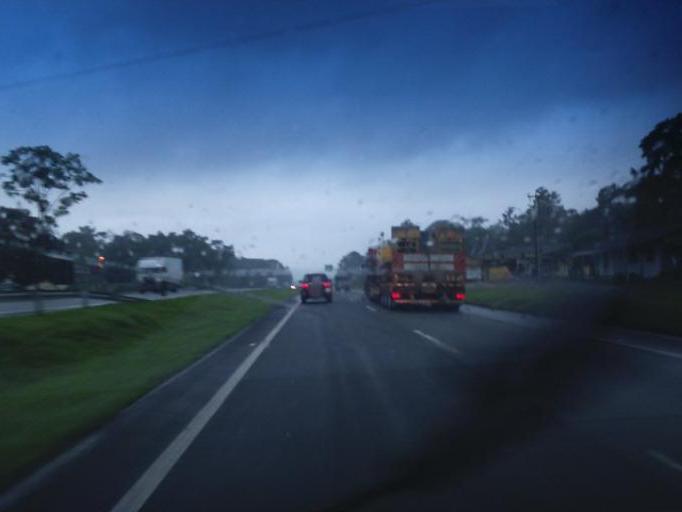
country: BR
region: Santa Catarina
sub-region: Joinville
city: Joinville
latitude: -26.0204
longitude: -48.8622
